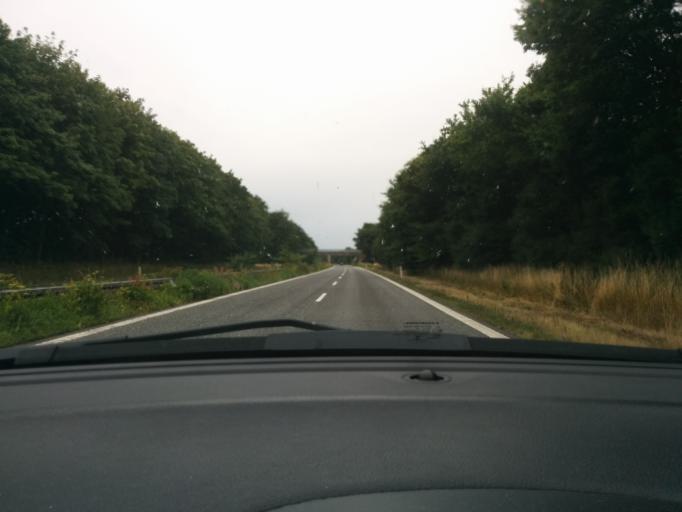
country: DK
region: Zealand
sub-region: Lolland Kommune
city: Maribo
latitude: 54.7897
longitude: 11.5259
